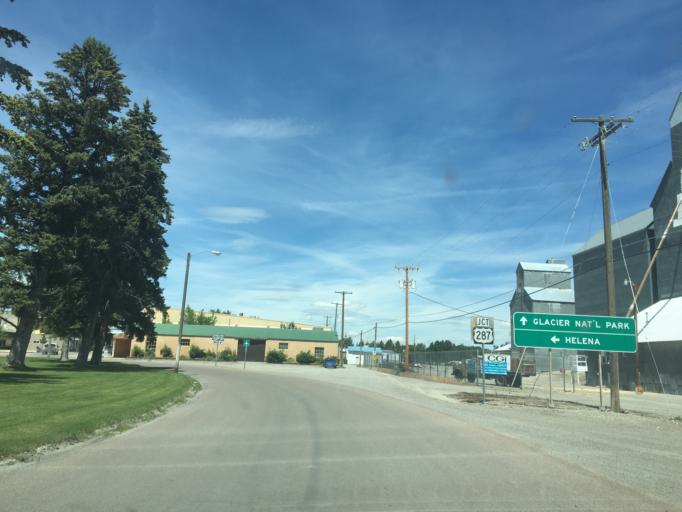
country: US
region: Montana
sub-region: Teton County
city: Choteau
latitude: 47.8108
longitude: -112.1816
